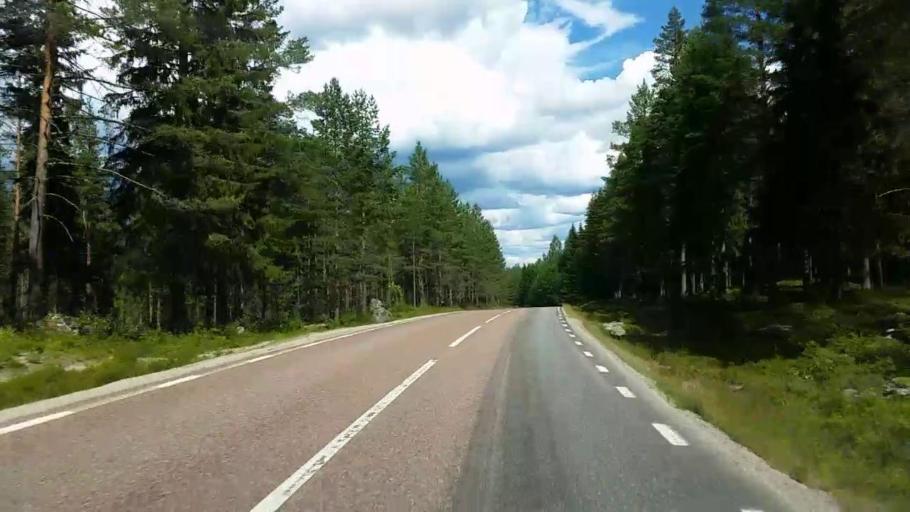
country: SE
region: Gaevleborg
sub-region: Ovanakers Kommun
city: Edsbyn
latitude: 61.3215
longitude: 15.5134
